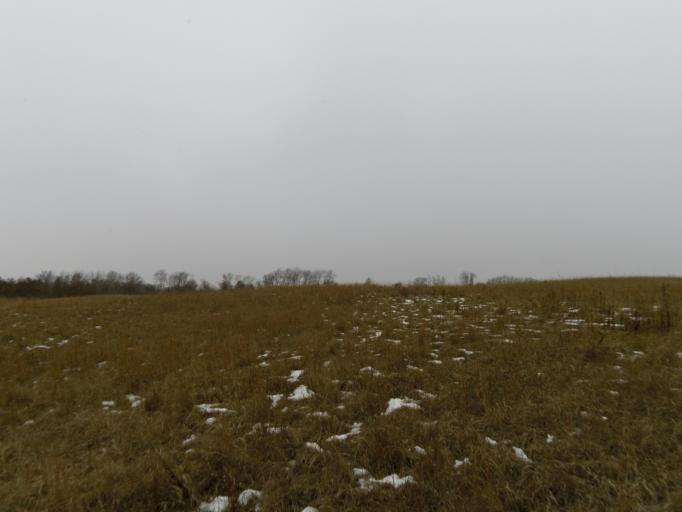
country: US
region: Minnesota
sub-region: Washington County
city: Lake Elmo
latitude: 44.9845
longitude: -92.9137
